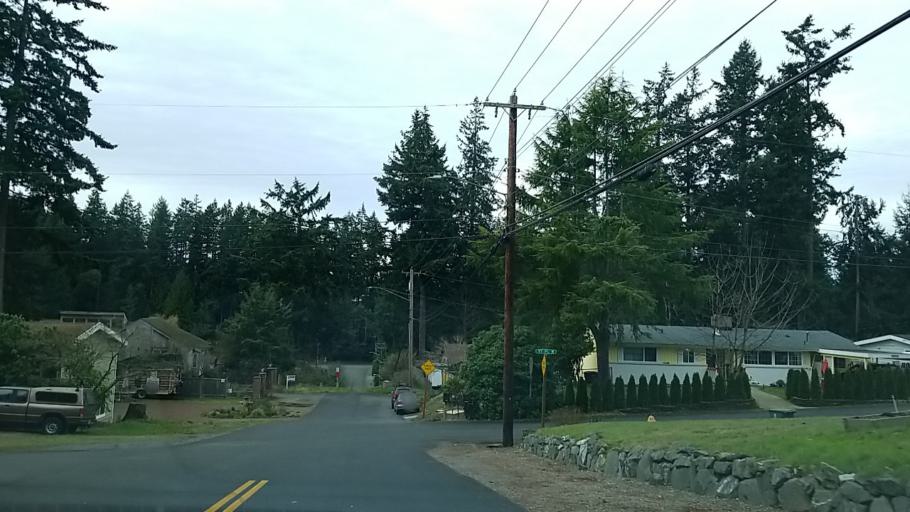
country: US
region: Washington
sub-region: Snohomish County
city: Esperance
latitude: 47.7869
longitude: -122.3632
